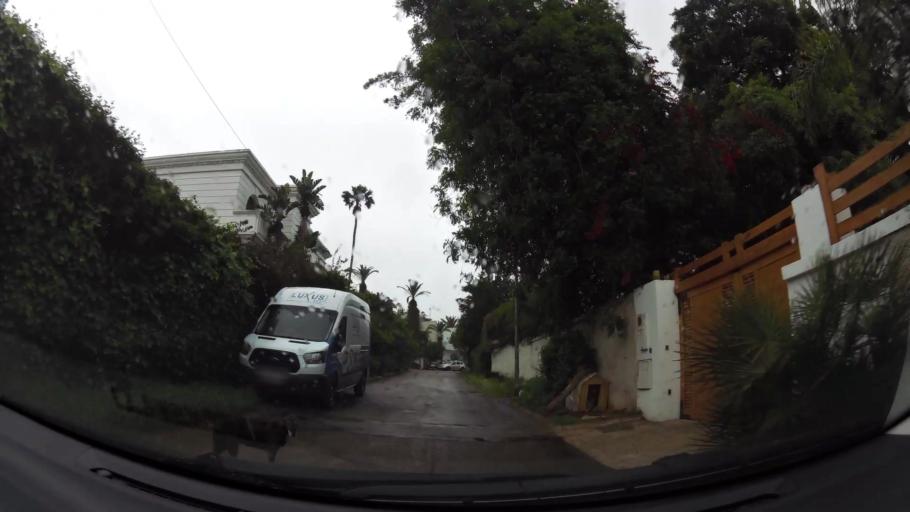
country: MA
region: Grand Casablanca
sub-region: Casablanca
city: Casablanca
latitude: 33.5903
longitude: -7.6600
